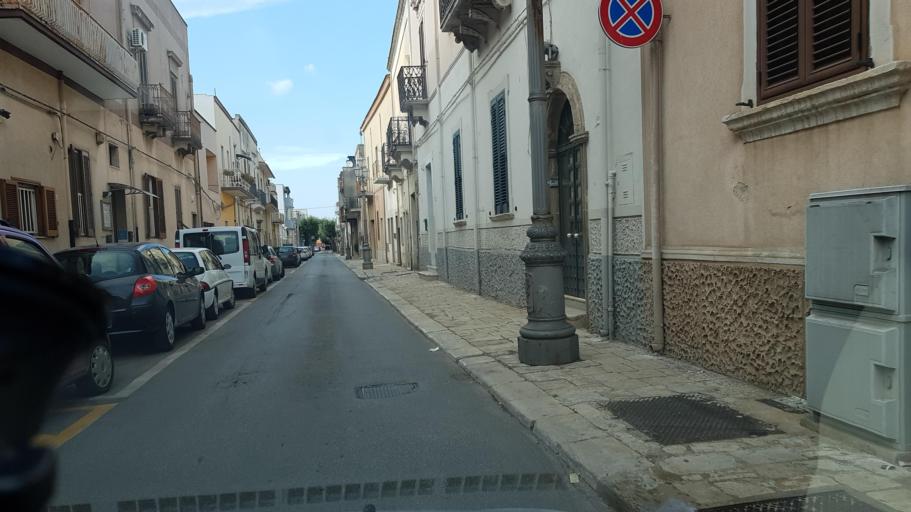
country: IT
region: Apulia
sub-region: Provincia di Brindisi
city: Latiano
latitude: 40.5544
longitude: 17.7189
